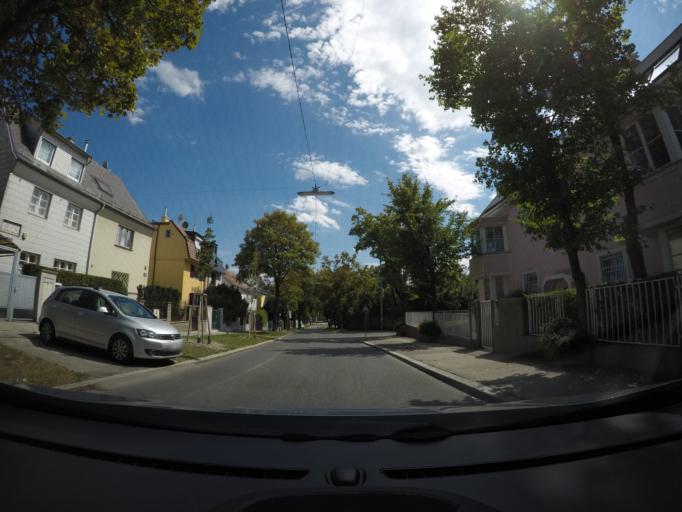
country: AT
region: Lower Austria
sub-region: Politischer Bezirk Modling
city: Perchtoldsdorf
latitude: 48.1825
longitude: 16.2644
